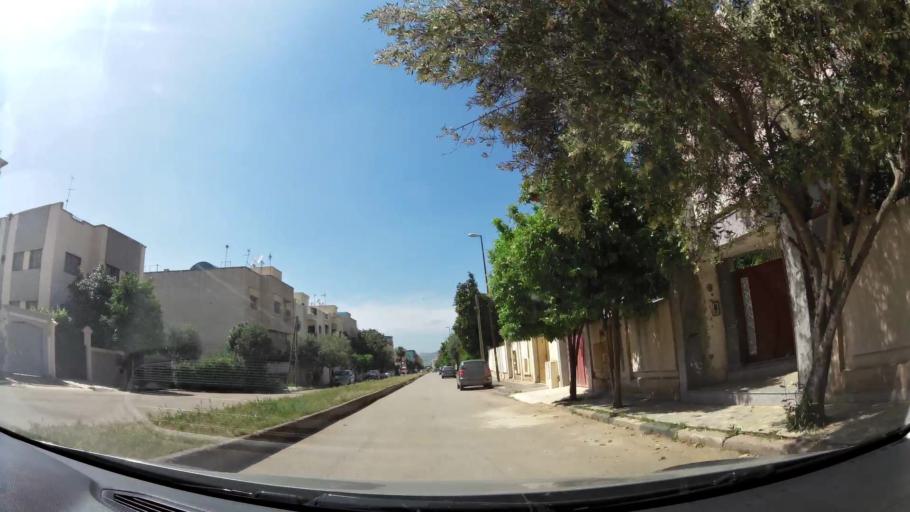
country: MA
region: Fes-Boulemane
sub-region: Fes
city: Fes
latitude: 34.0181
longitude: -5.0244
